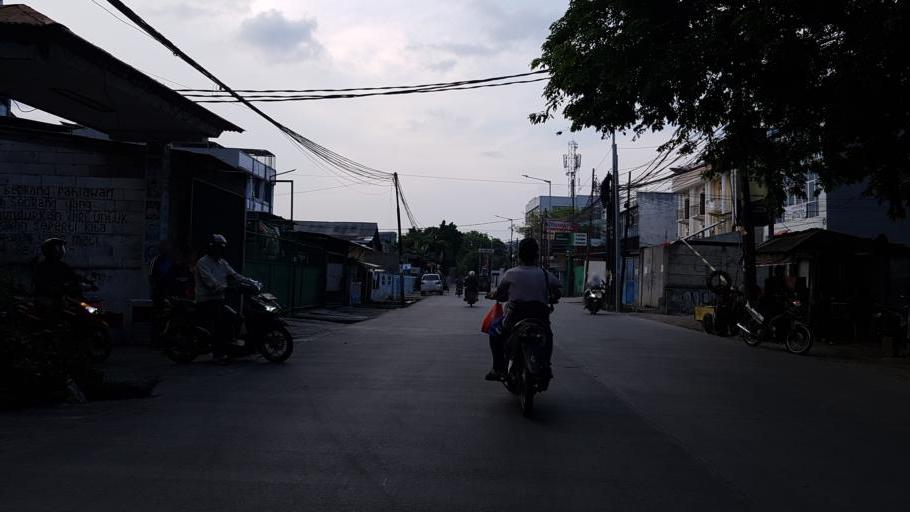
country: ID
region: West Java
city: Teluknaga
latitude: -6.1307
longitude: 106.7458
